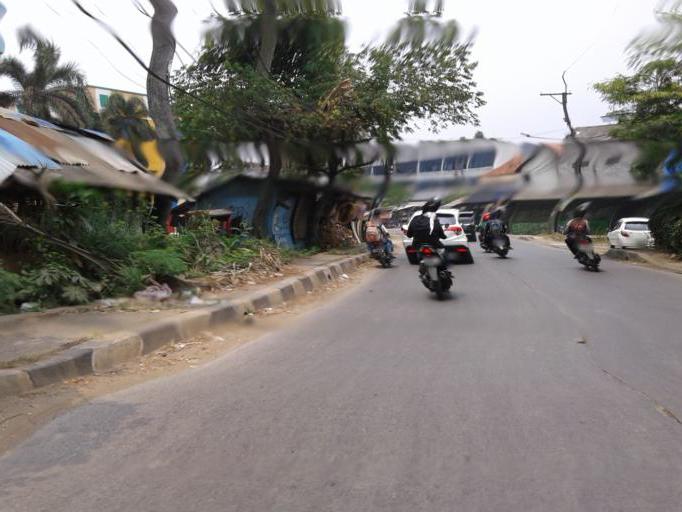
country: ID
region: West Java
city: Pamulang
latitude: -6.3248
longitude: 106.7443
